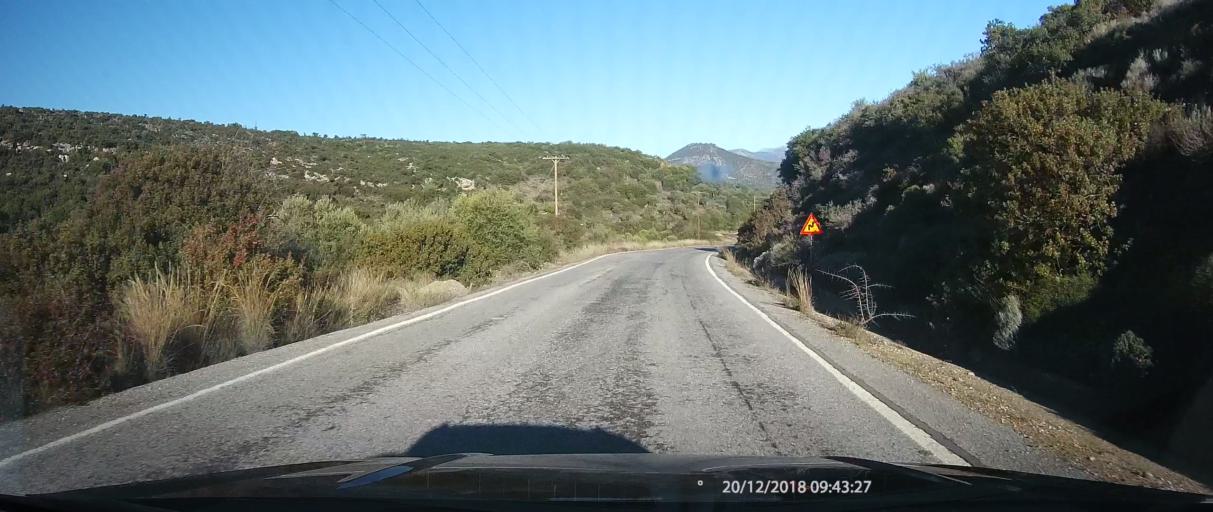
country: GR
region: Peloponnese
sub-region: Nomos Lakonias
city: Yerakion
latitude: 36.9651
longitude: 22.7442
